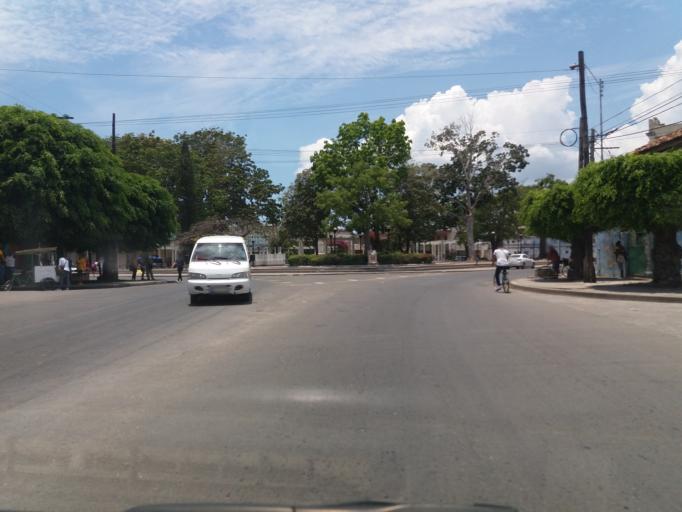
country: CU
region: Cienfuegos
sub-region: Municipio de Cienfuegos
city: Cienfuegos
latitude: 22.1491
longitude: -80.4448
